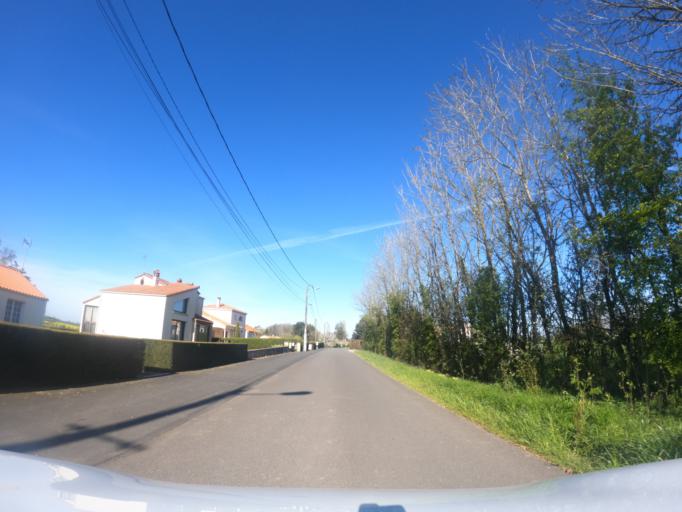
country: FR
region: Pays de la Loire
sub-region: Departement de la Vendee
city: Saint-Pierre-du-Chemin
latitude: 46.6895
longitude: -0.7037
